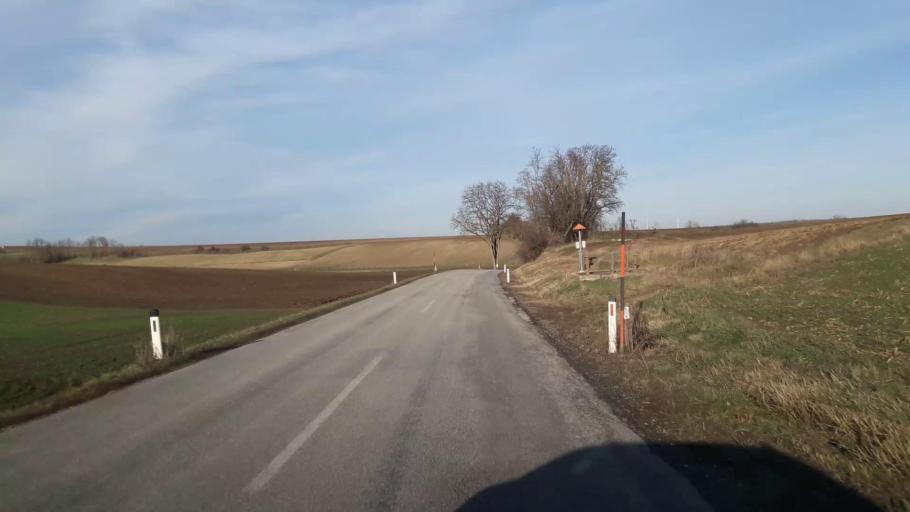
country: AT
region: Lower Austria
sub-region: Politischer Bezirk Ganserndorf
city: Auersthal
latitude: 48.3877
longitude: 16.6312
